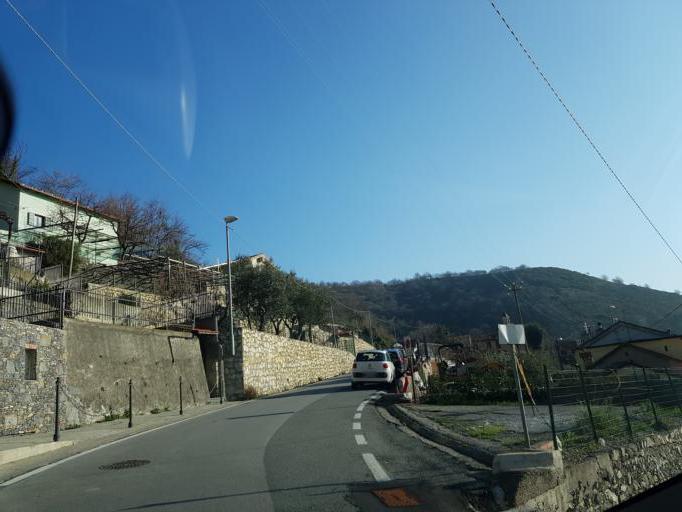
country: IT
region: Liguria
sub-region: Provincia di Genova
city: Piccarello
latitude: 44.4598
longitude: 8.9516
